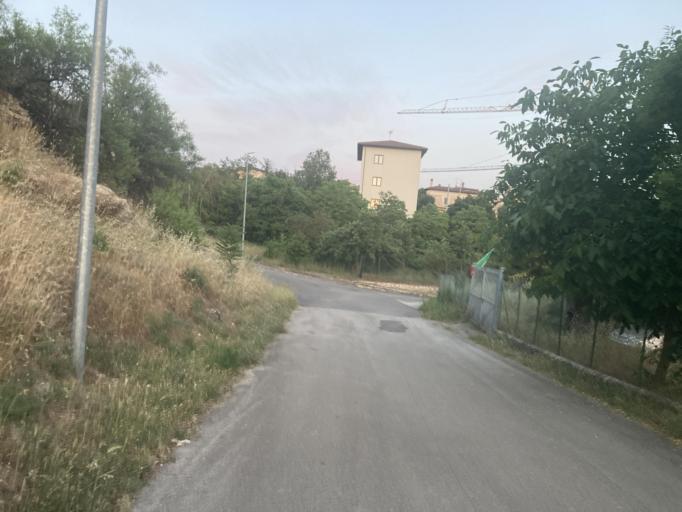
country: IT
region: Abruzzo
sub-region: Provincia dell' Aquila
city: San Demetrio Ne' Vestini
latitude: 42.2925
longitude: 13.5529
